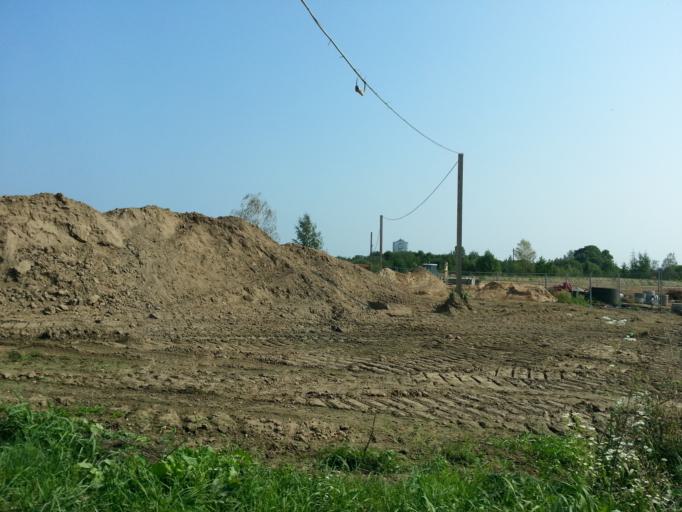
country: LT
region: Vilnius County
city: Pasilaiciai
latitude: 54.7289
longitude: 25.2060
